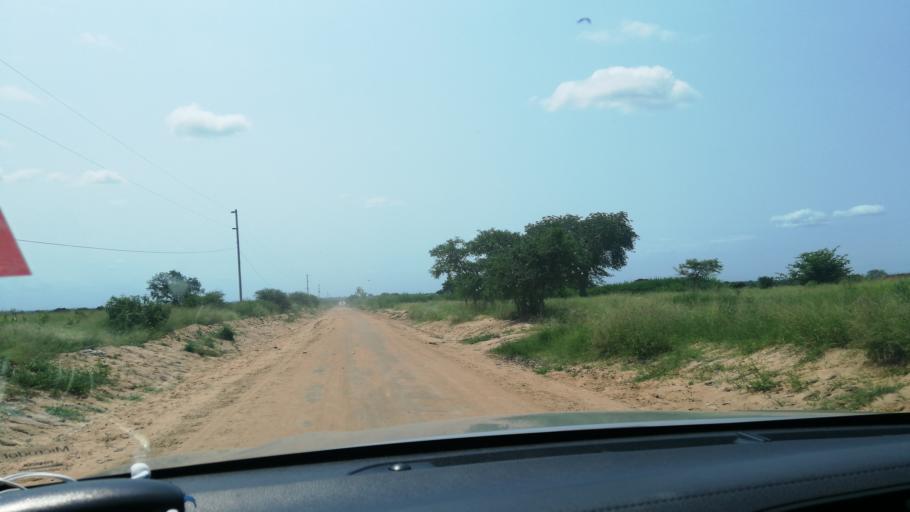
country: MZ
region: Maputo
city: Matola
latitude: -26.0978
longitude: 32.3889
